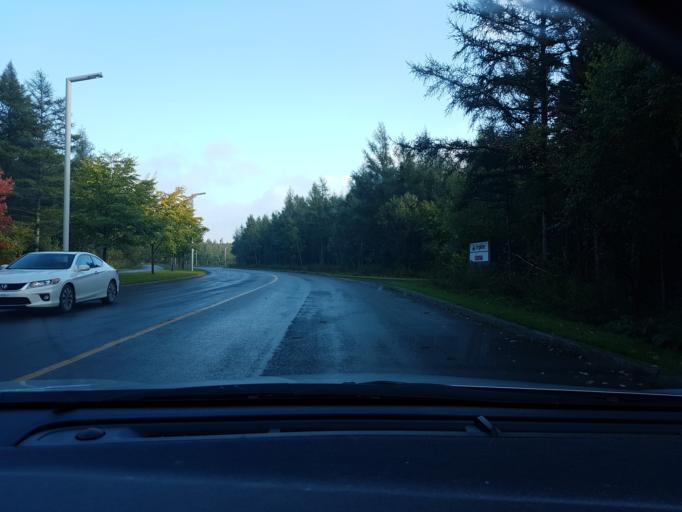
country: CA
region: Quebec
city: L'Ancienne-Lorette
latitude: 46.7995
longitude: -71.3170
